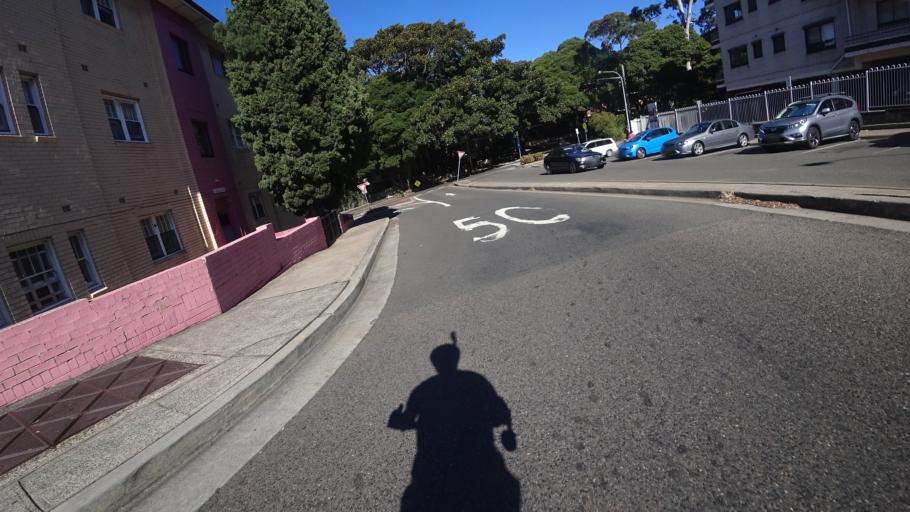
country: AU
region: New South Wales
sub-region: Rockdale
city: Banksia
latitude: -33.9533
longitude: 151.1356
